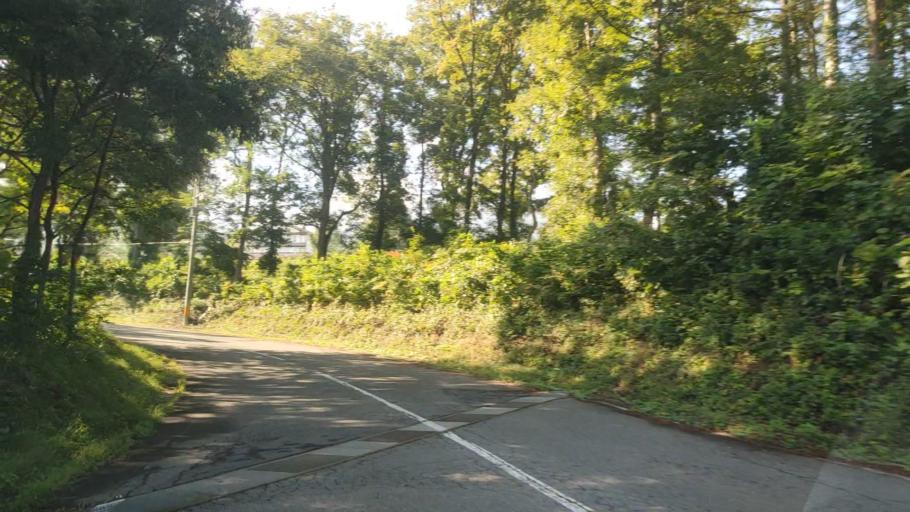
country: JP
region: Nagano
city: Iiyama
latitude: 36.8288
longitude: 138.4056
